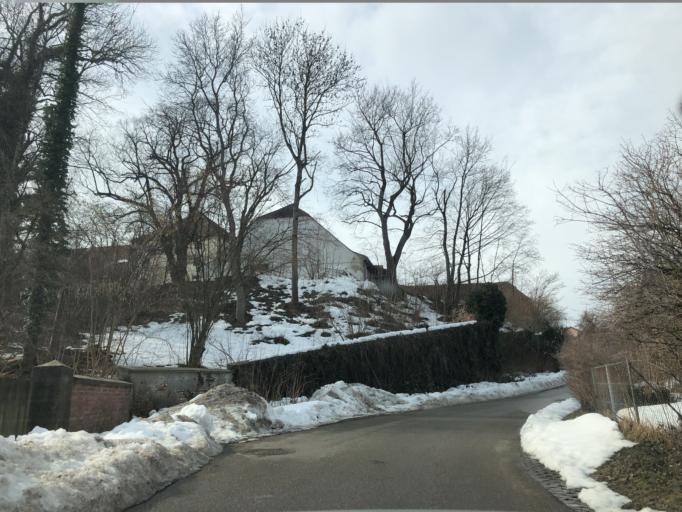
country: DE
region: Bavaria
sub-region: Upper Bavaria
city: Ebersberg
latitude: 48.0788
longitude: 11.9724
